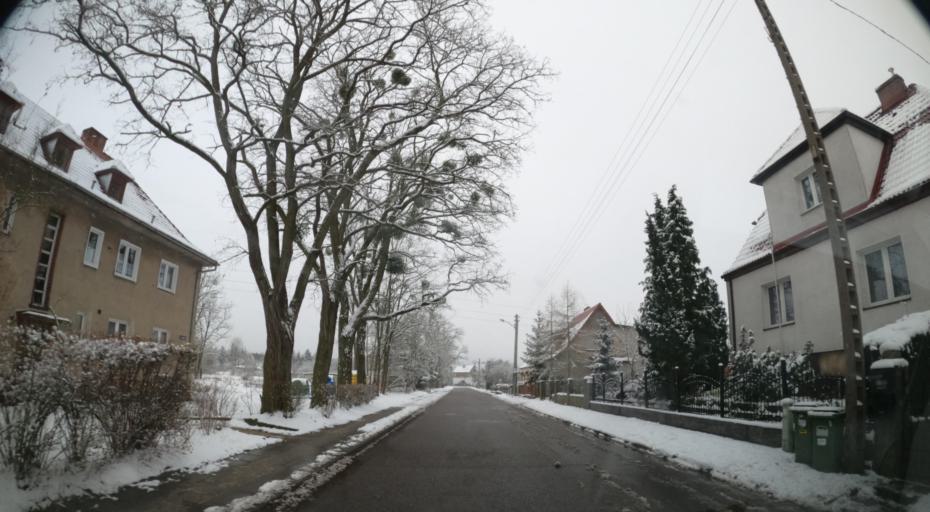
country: PL
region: West Pomeranian Voivodeship
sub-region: Szczecin
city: Szczecin
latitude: 53.3450
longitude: 14.5749
